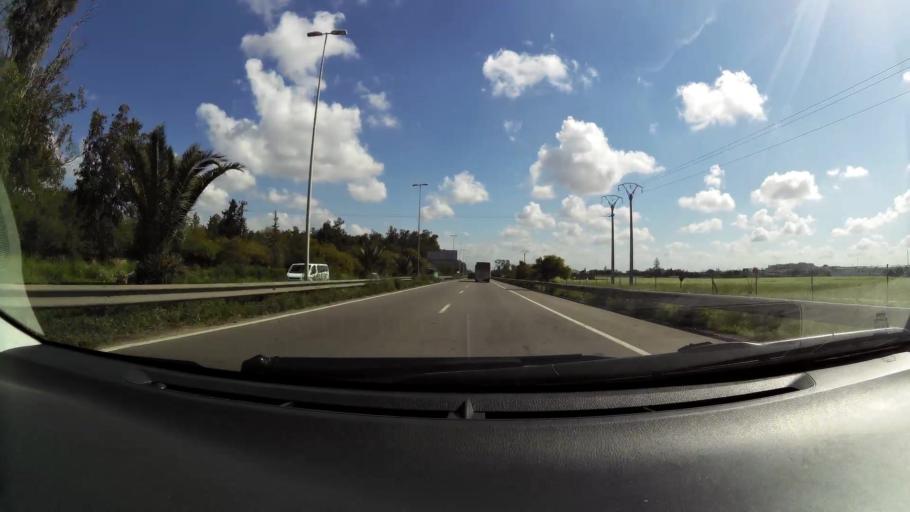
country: MA
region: Grand Casablanca
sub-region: Nouaceur
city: Bouskoura
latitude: 33.4781
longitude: -7.6335
